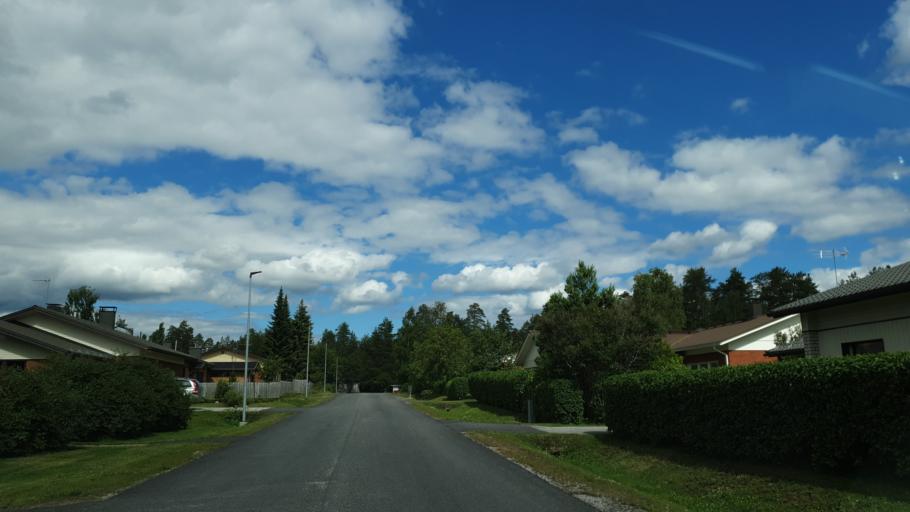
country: FI
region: Kainuu
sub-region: Kehys-Kainuu
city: Kuhmo
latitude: 64.1199
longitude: 29.5392
